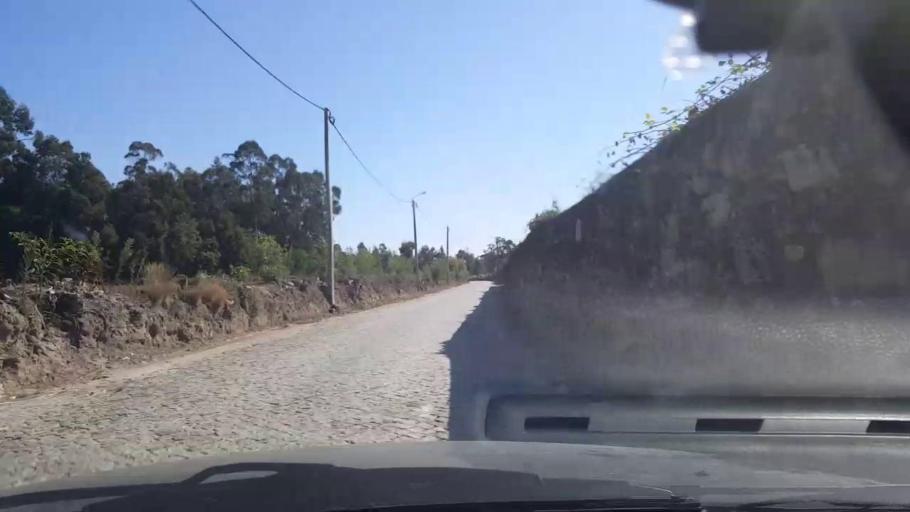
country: PT
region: Porto
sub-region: Vila do Conde
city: Arvore
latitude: 41.3151
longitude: -8.6880
